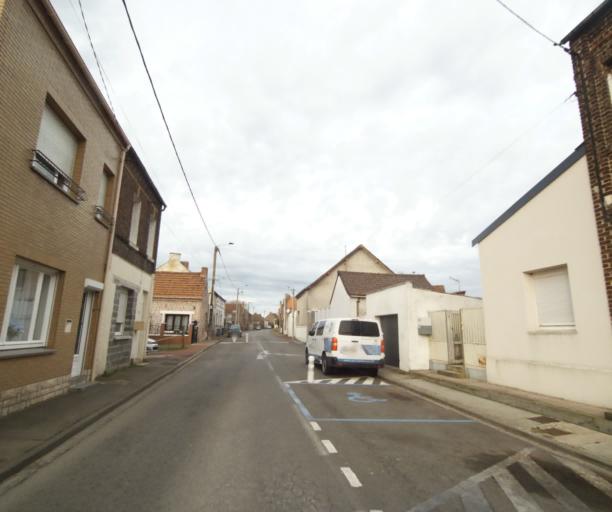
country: FR
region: Nord-Pas-de-Calais
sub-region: Departement du Nord
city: Hergnies
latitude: 50.4668
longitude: 3.5457
